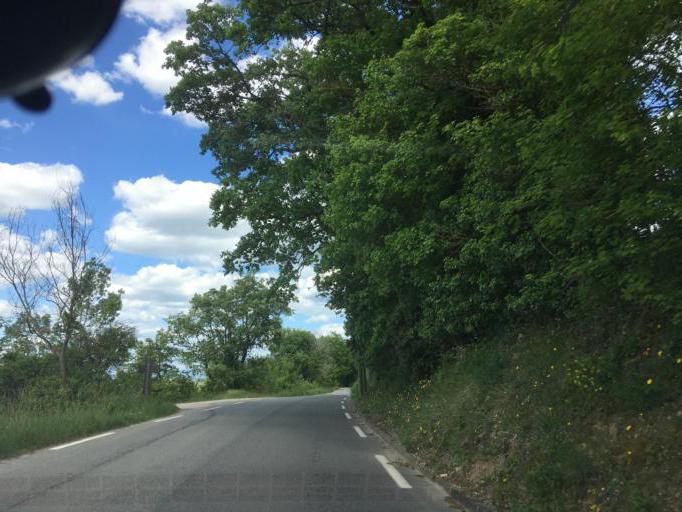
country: FR
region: Provence-Alpes-Cote d'Azur
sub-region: Departement du Var
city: Ginasservis
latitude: 43.5931
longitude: 5.8553
